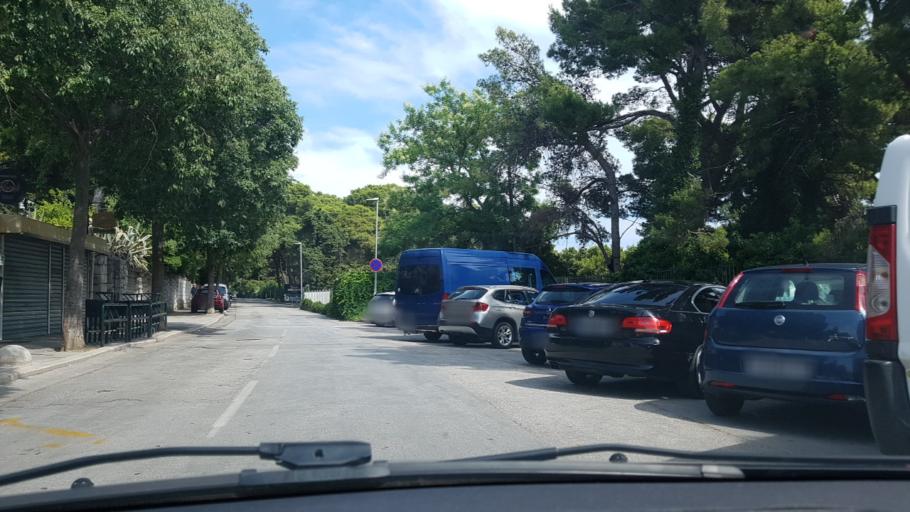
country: HR
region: Splitsko-Dalmatinska
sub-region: Grad Split
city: Split
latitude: 43.5015
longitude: 16.4504
